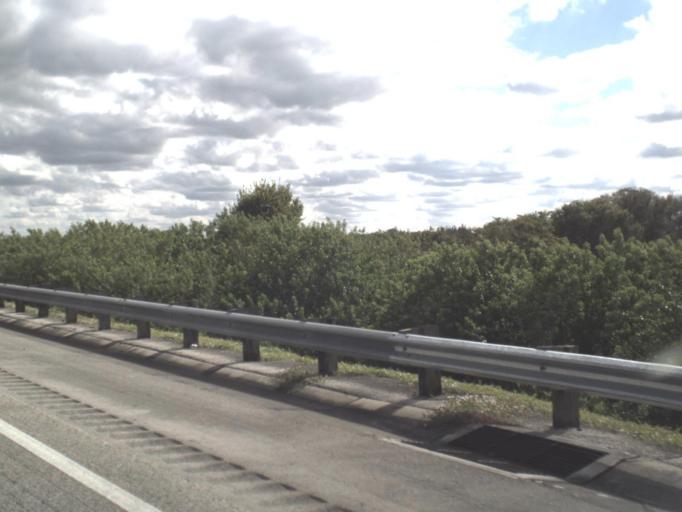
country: US
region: Florida
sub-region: Saint Lucie County
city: Fort Pierce South
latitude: 27.4134
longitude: -80.4025
